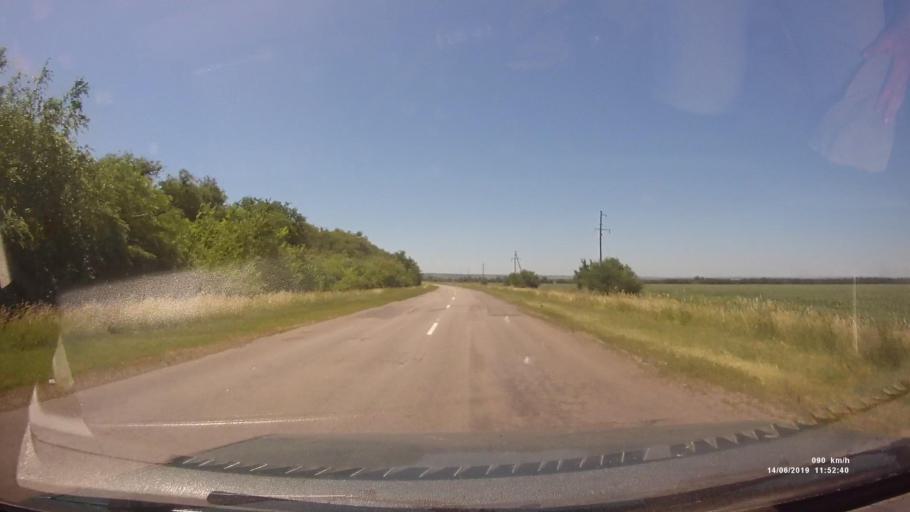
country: RU
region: Rostov
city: Kazanskaya
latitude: 49.8340
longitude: 41.2247
